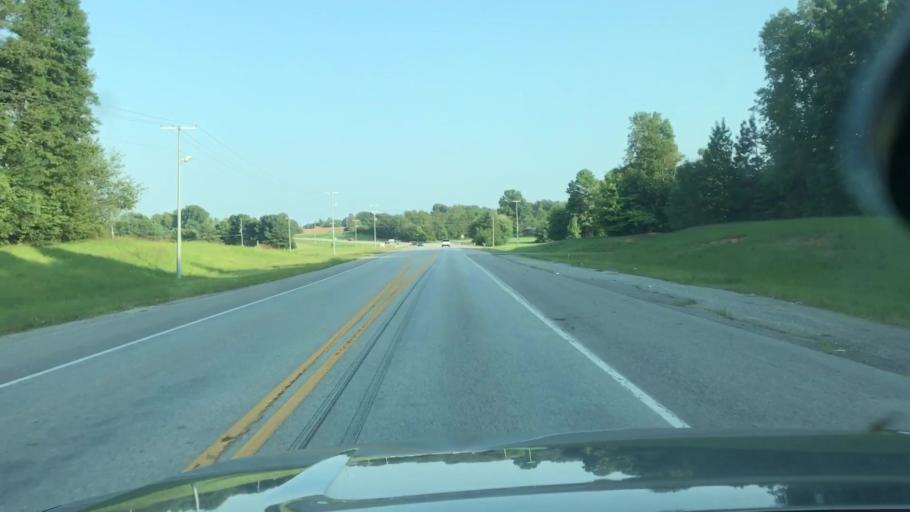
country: US
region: Tennessee
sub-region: Sumner County
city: Portland
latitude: 36.5874
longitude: -86.5873
